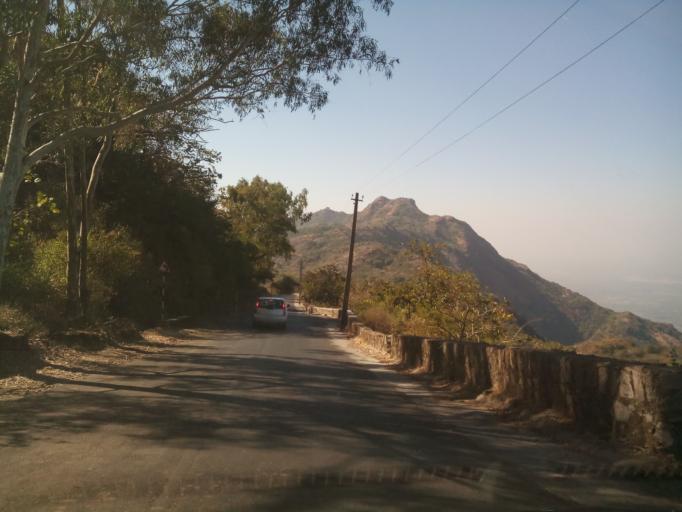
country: IN
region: Rajasthan
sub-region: Sirohi
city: Abu
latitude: 24.6304
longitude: 72.7474
